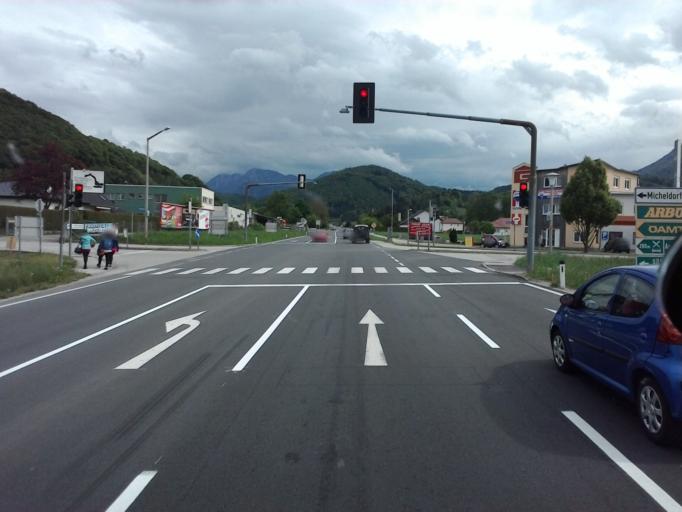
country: AT
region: Upper Austria
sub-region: Politischer Bezirk Kirchdorf an der Krems
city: Micheldorf in Oberoesterreich
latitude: 47.8763
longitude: 14.1291
